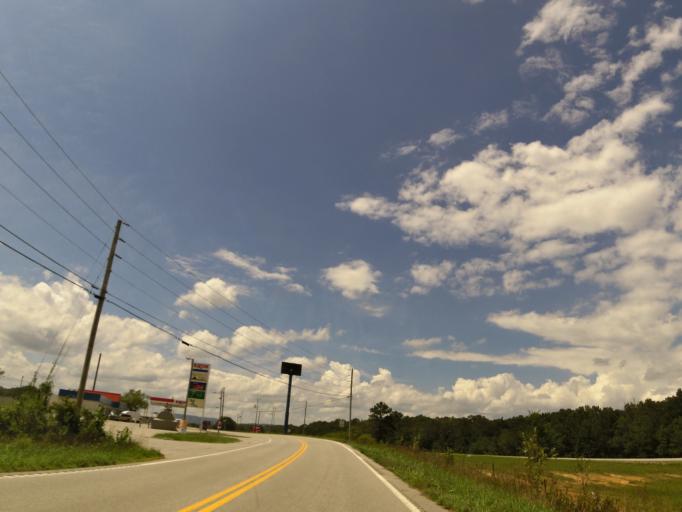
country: US
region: Tennessee
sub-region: Roane County
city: Rockwood
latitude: 35.8914
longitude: -84.7358
